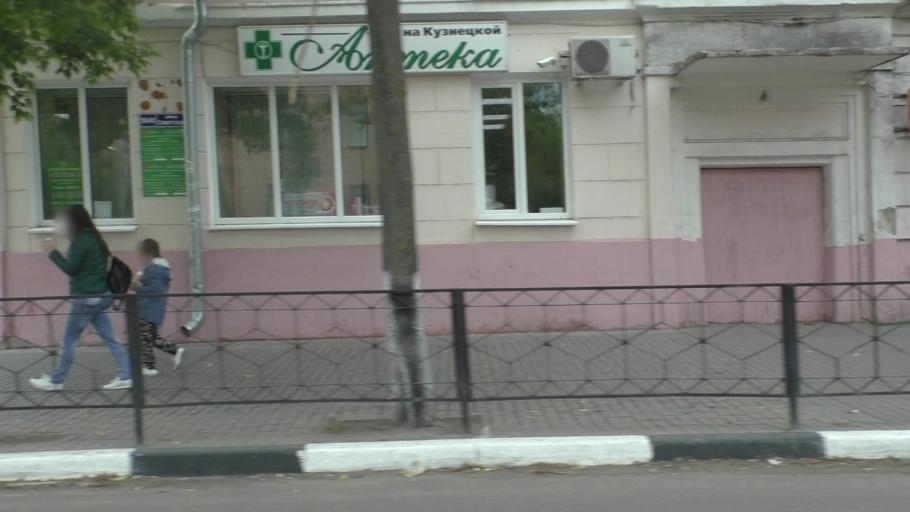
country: RU
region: Moskovskaya
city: Yegor'yevsk
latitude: 55.3770
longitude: 39.0450
